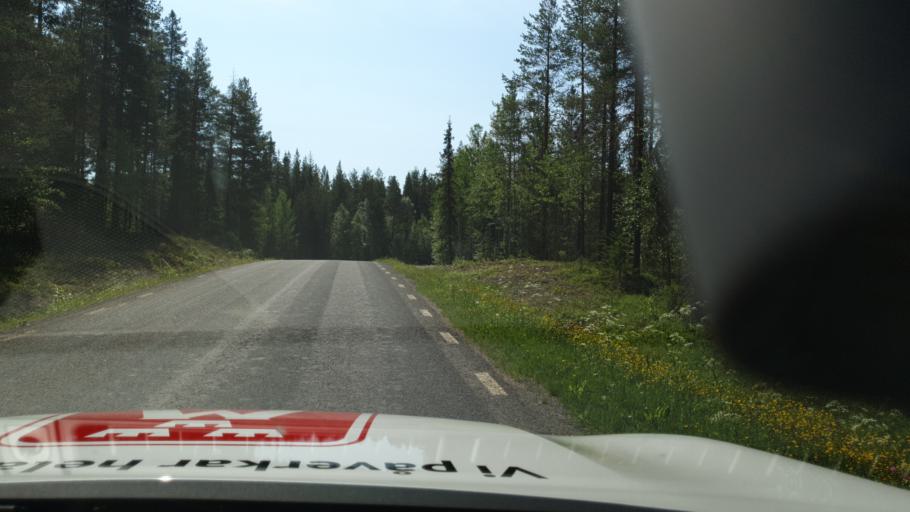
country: SE
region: Vaesterbotten
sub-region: Skelleftea Kommun
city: Langsele
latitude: 65.0031
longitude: 20.0910
